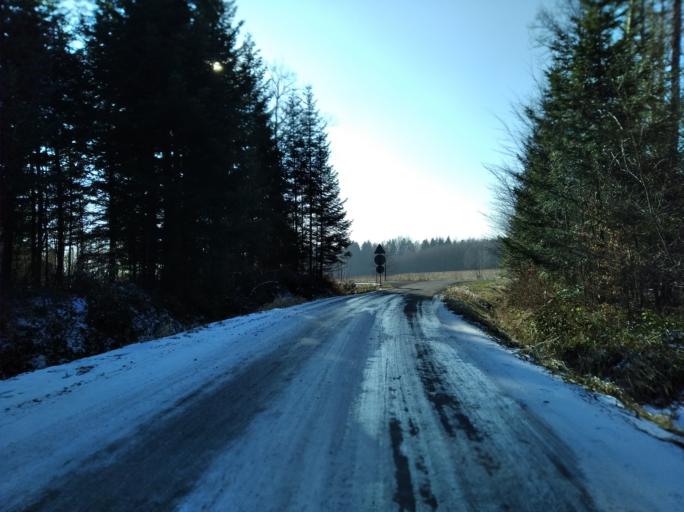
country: PL
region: Subcarpathian Voivodeship
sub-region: Powiat rzeszowski
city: Straszydle
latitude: 49.8642
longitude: 21.9681
